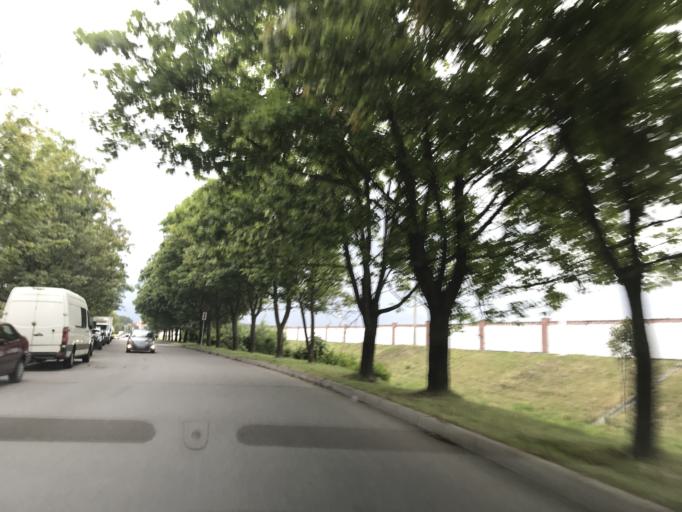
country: BY
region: Minsk
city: Borovlyany
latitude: 53.9604
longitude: 27.6231
